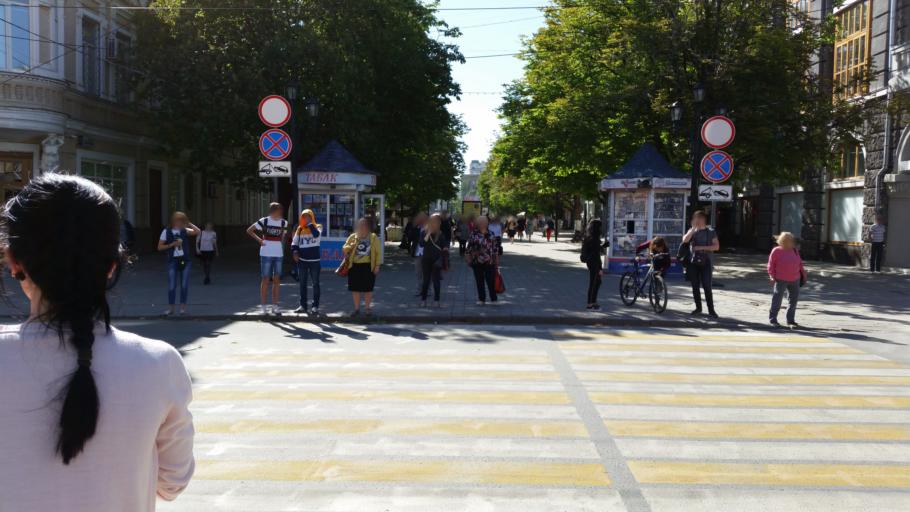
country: RU
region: Saratov
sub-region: Saratovskiy Rayon
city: Saratov
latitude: 51.5321
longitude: 46.0245
